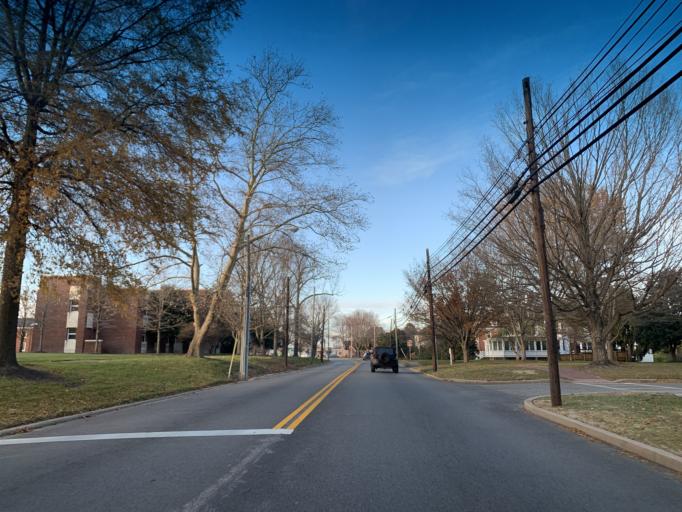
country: US
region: Maryland
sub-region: Kent County
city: Chestertown
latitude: 39.2178
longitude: -76.0669
